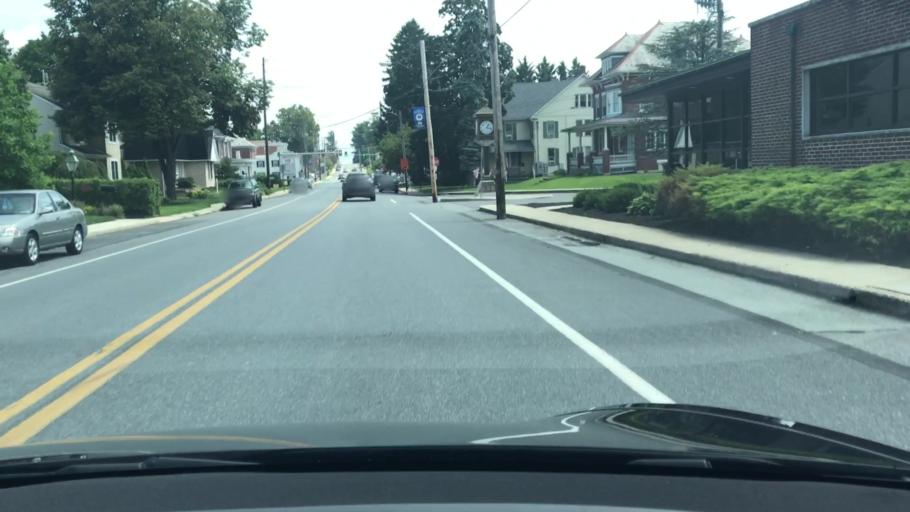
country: US
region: Pennsylvania
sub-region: Lancaster County
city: Landisville
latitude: 40.0959
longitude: -76.4120
